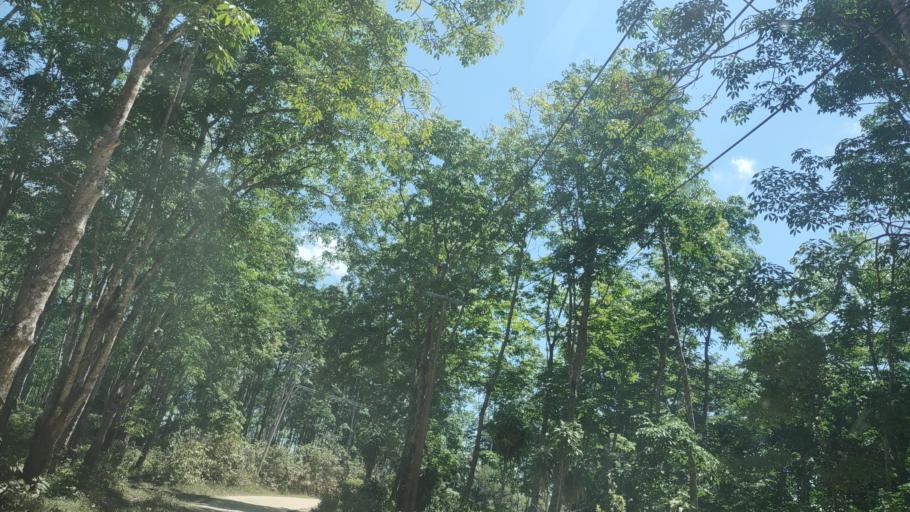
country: MX
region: Veracruz
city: Las Choapas
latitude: 17.7740
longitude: -94.1466
